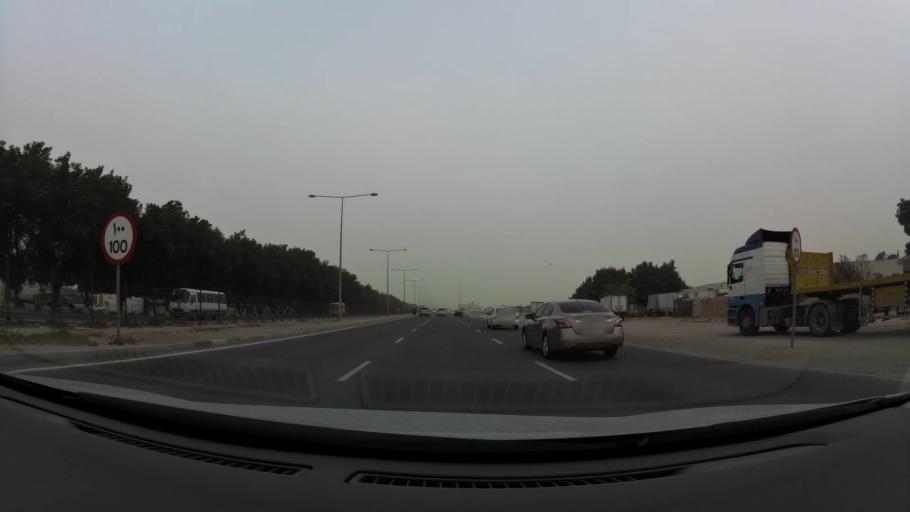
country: QA
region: Baladiyat ad Dawhah
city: Doha
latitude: 25.2388
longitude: 51.4797
